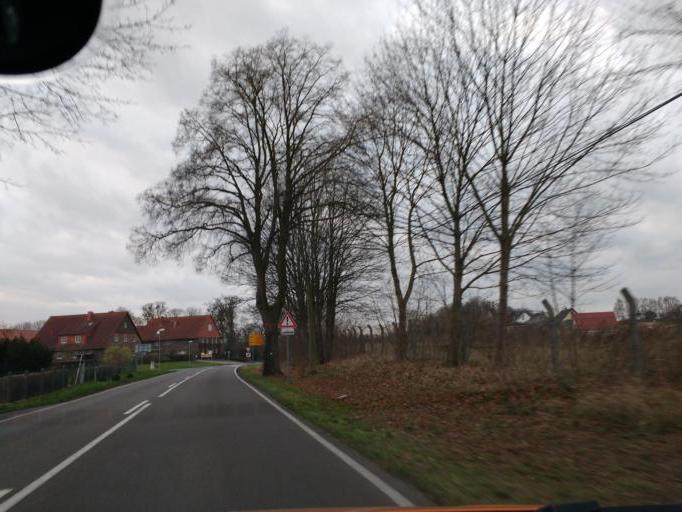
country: DE
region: Brandenburg
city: Protzel
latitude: 52.6384
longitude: 13.9922
